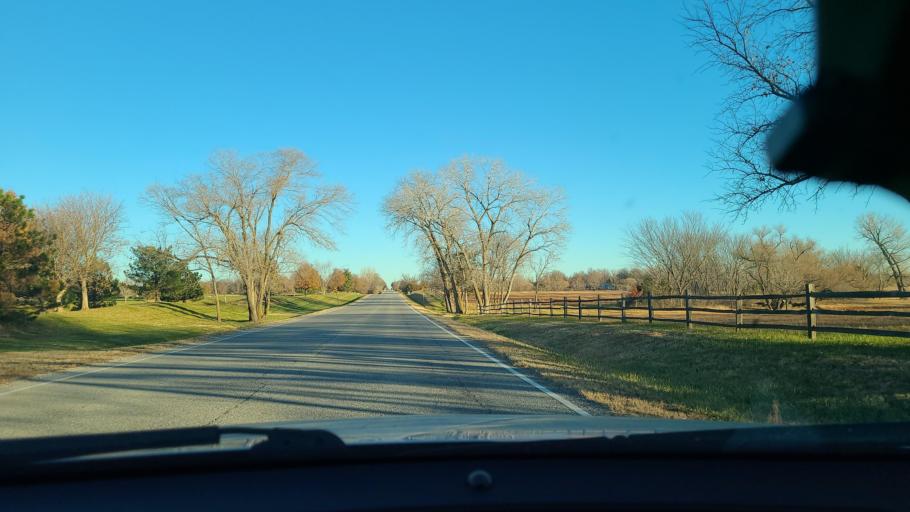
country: US
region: Kansas
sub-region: Sedgwick County
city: Park City
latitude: 37.8429
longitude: -97.3174
